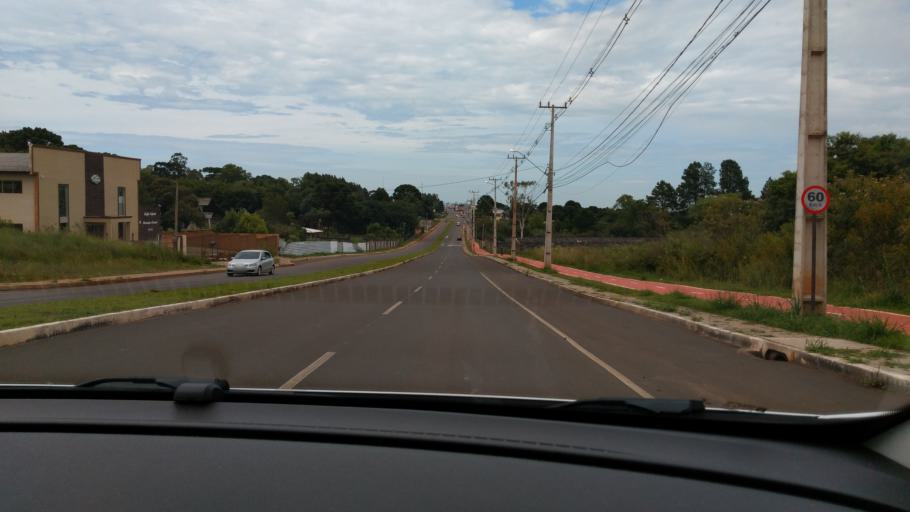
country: BR
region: Parana
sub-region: Guarapuava
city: Guarapuava
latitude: -25.3679
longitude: -51.4372
